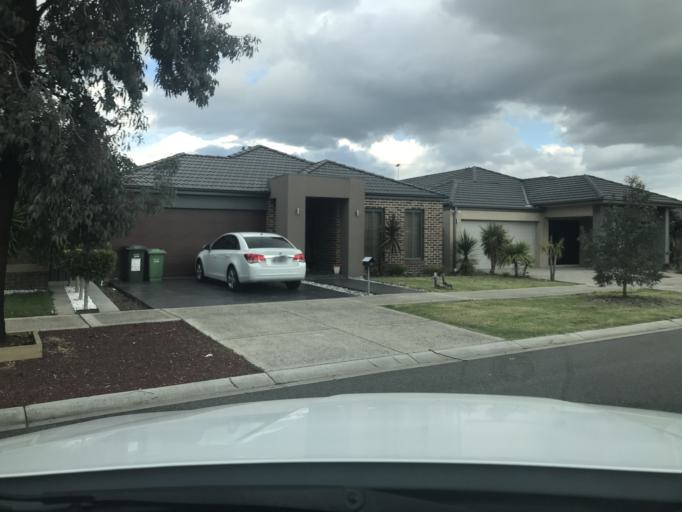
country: AU
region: Victoria
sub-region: Hume
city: Craigieburn
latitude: -37.5820
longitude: 144.9104
